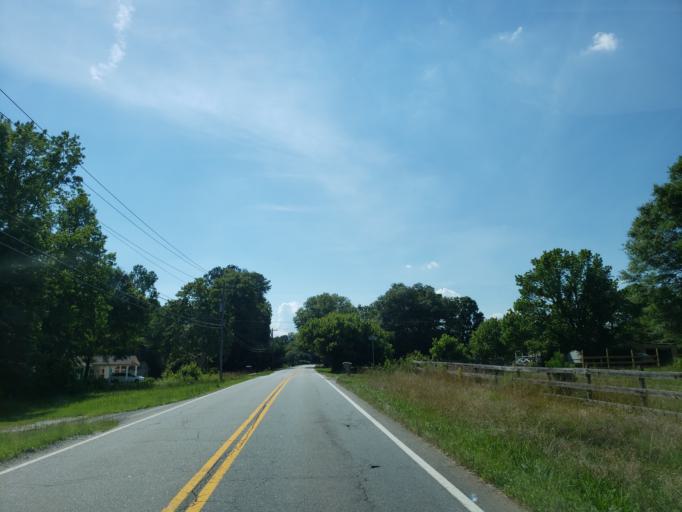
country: US
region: Georgia
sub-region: Cherokee County
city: Woodstock
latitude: 34.1108
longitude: -84.4527
